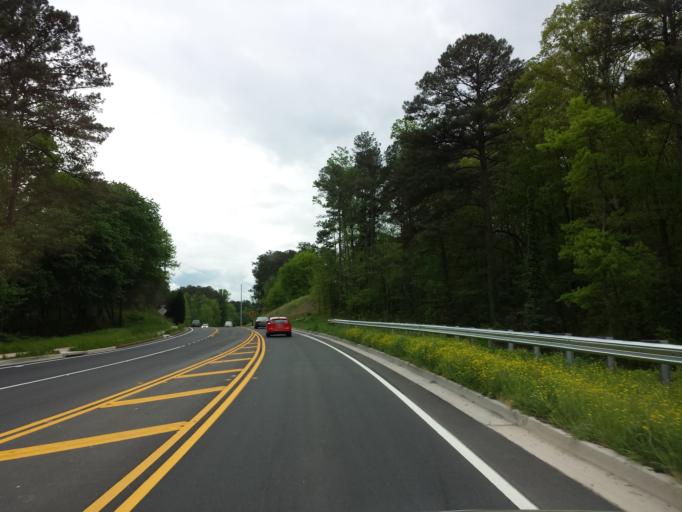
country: US
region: Georgia
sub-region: Cherokee County
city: Woodstock
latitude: 34.0617
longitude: -84.5612
